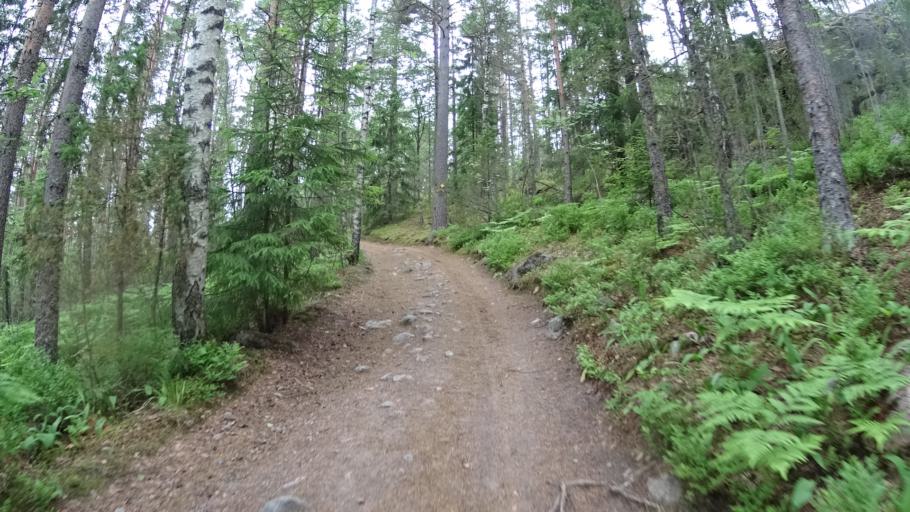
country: FI
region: Uusimaa
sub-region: Helsinki
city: Espoo
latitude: 60.2938
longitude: 24.5216
